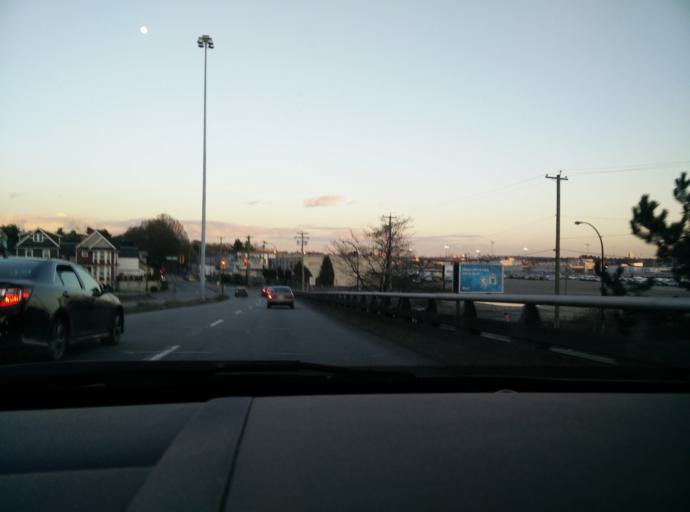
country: CA
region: British Columbia
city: Vancouver
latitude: 49.2770
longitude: -123.0982
